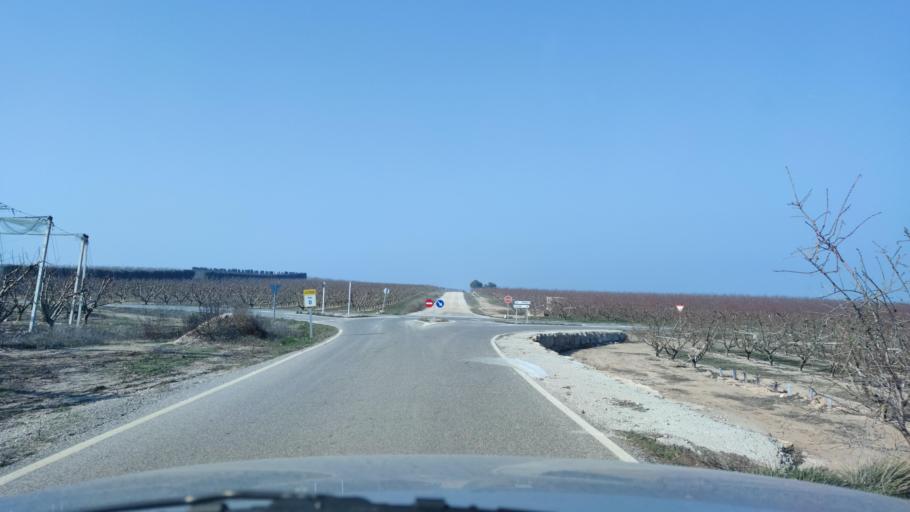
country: ES
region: Catalonia
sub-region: Provincia de Lleida
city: Sunyer
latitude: 41.5315
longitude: 0.5759
